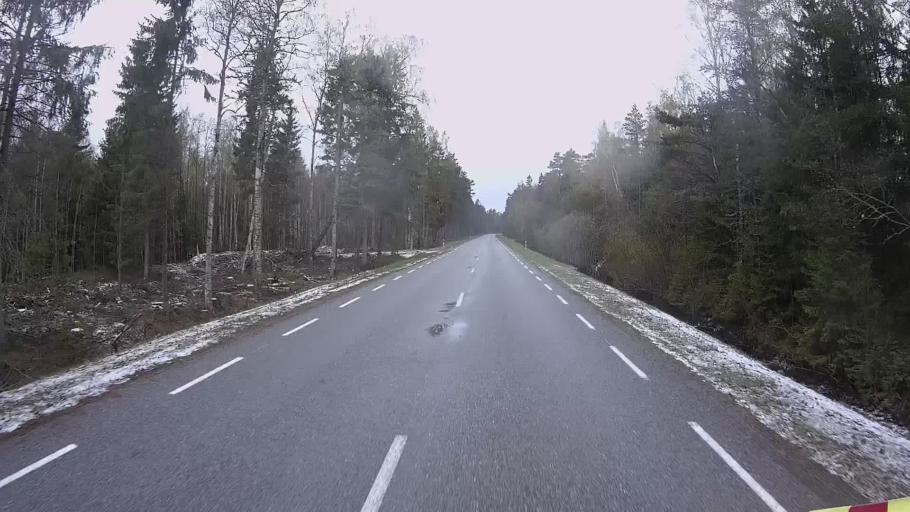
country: EE
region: Hiiumaa
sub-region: Kaerdla linn
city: Kardla
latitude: 59.0431
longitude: 22.6816
